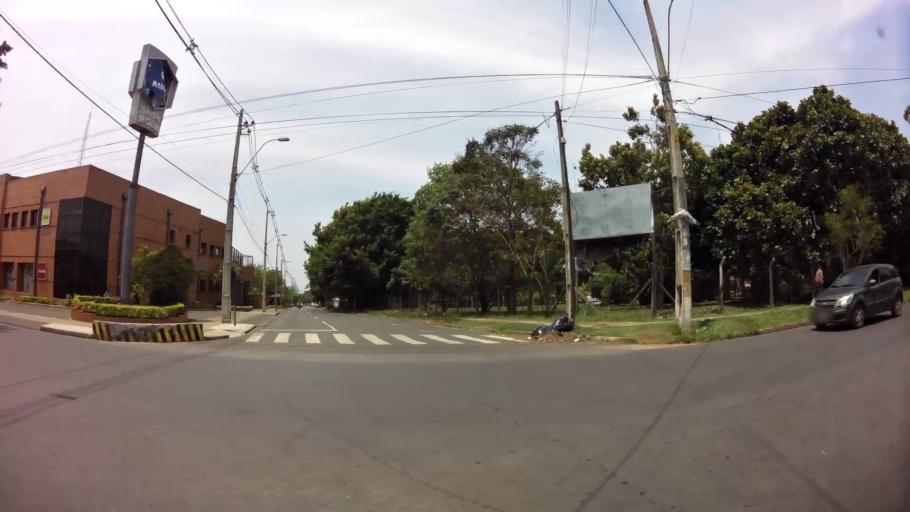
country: PY
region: Central
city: Lambare
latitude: -25.3129
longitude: -57.5712
